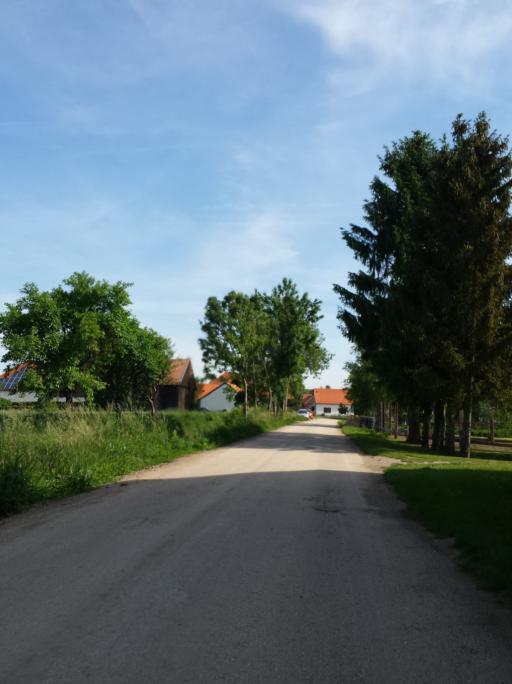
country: AT
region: Lower Austria
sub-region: Politischer Bezirk Hollabrunn
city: Wullersdorf
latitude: 48.6456
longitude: 16.1258
